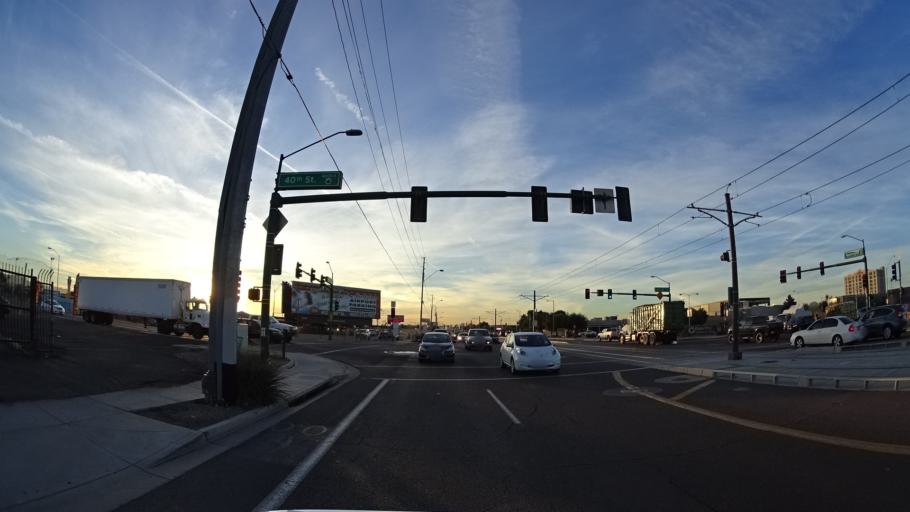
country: US
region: Arizona
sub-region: Maricopa County
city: Tempe Junction
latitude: 33.4480
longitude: -111.9952
